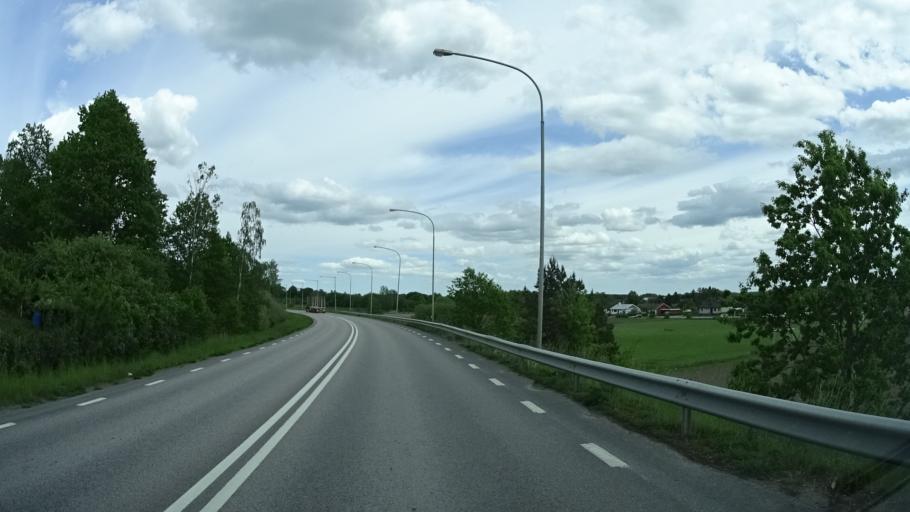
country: SE
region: OEstergoetland
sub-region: Norrkopings Kommun
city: Skarblacka
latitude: 58.5801
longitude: 15.9303
